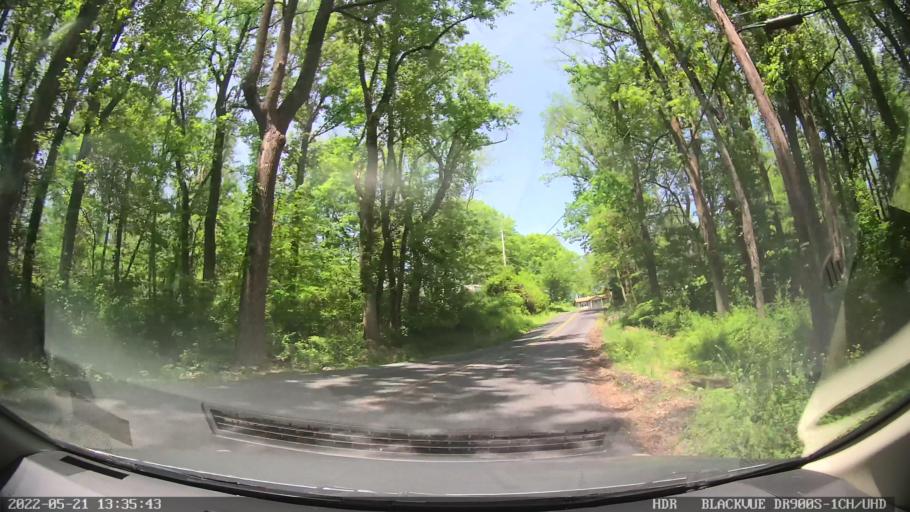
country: US
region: Pennsylvania
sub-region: Berks County
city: Topton
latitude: 40.4498
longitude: -75.6791
